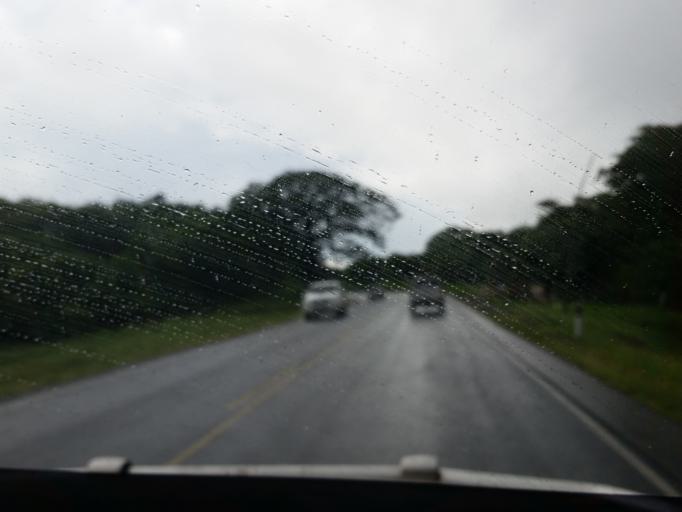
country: NI
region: Matagalpa
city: Ciudad Dario
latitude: 12.5685
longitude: -86.0490
